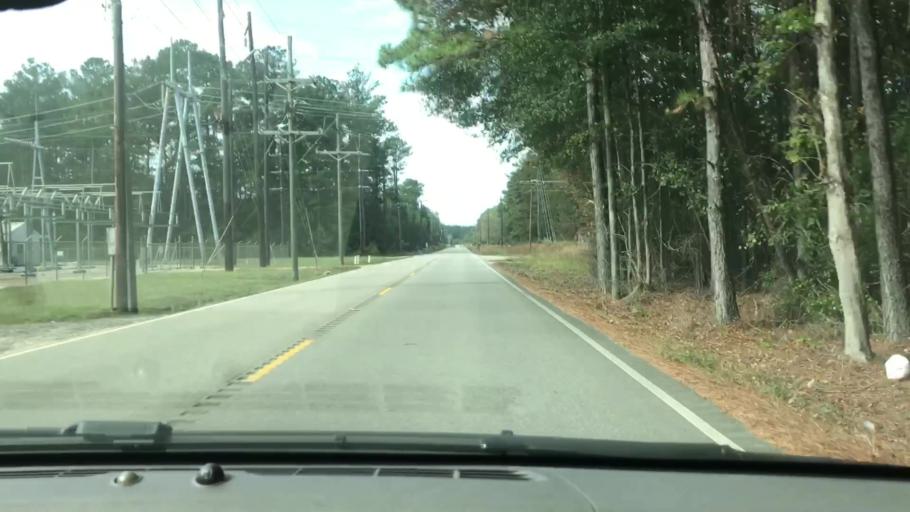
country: US
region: Louisiana
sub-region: Saint Tammany Parish
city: Abita Springs
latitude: 30.5344
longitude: -89.8889
